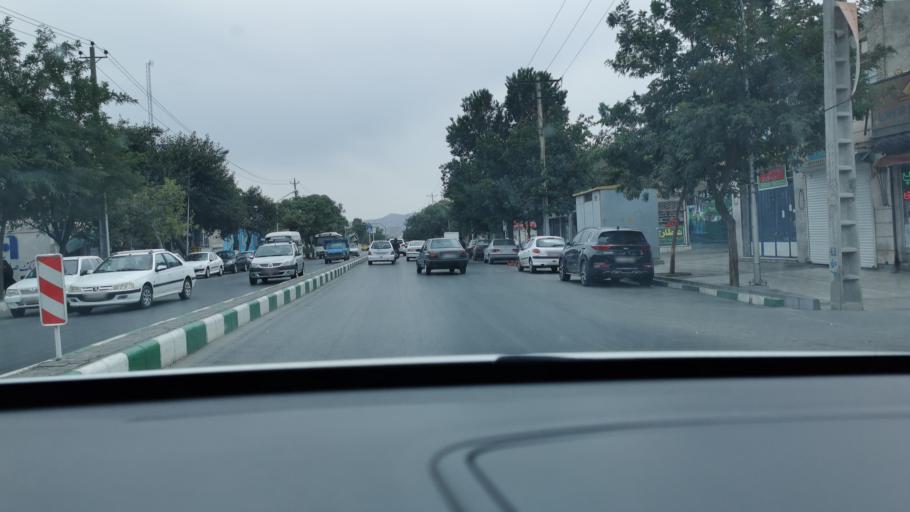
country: IR
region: Razavi Khorasan
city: Mashhad
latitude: 36.3158
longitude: 59.6170
